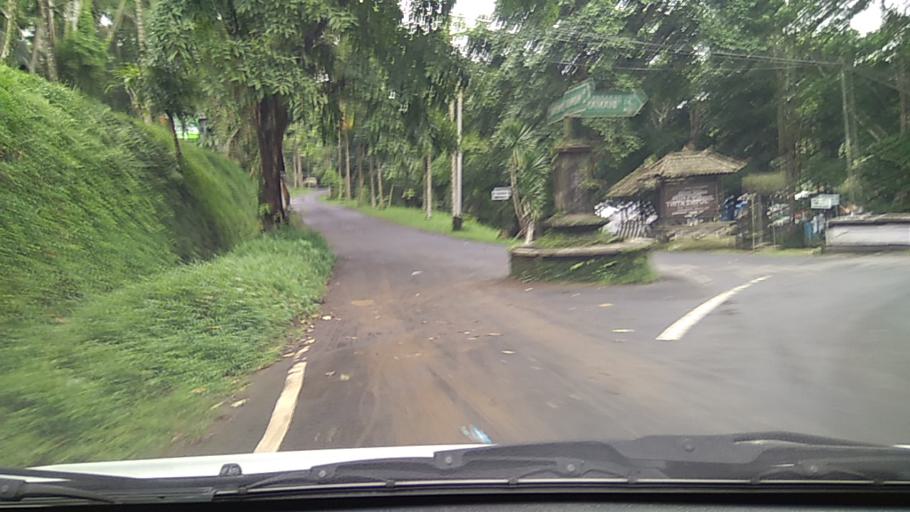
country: ID
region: Bali
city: Banjar Manukayaanyar
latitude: -8.4175
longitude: 115.3137
